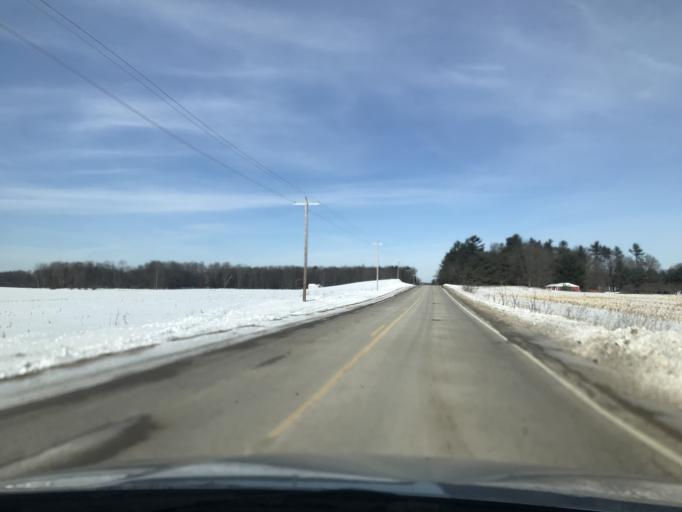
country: US
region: Wisconsin
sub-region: Oconto County
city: Oconto Falls
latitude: 45.1329
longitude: -88.1776
